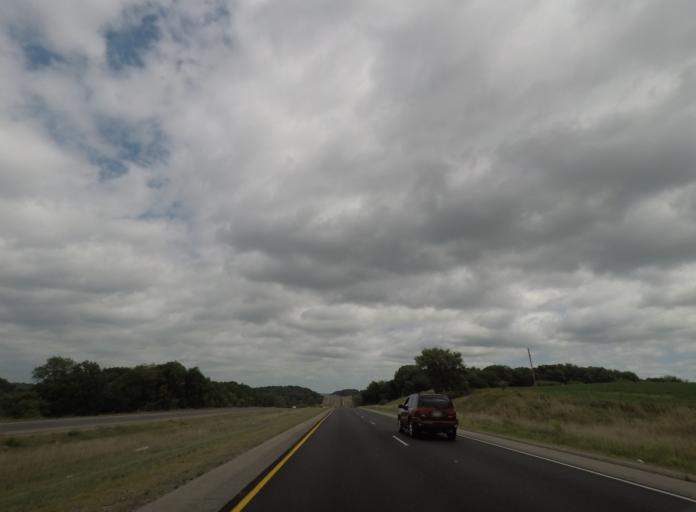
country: US
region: Iowa
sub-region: Linn County
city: Ely
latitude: 41.9256
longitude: -91.5869
